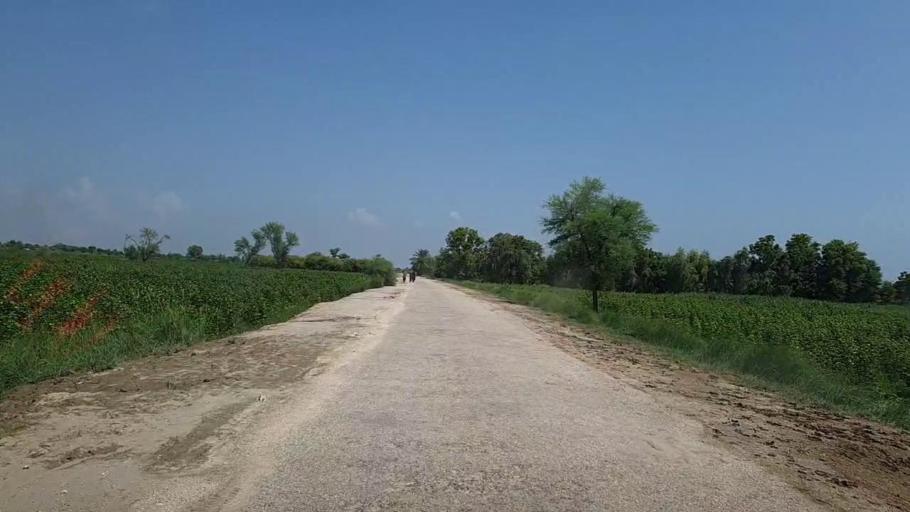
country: PK
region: Sindh
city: Bhiria
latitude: 26.8952
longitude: 68.2216
